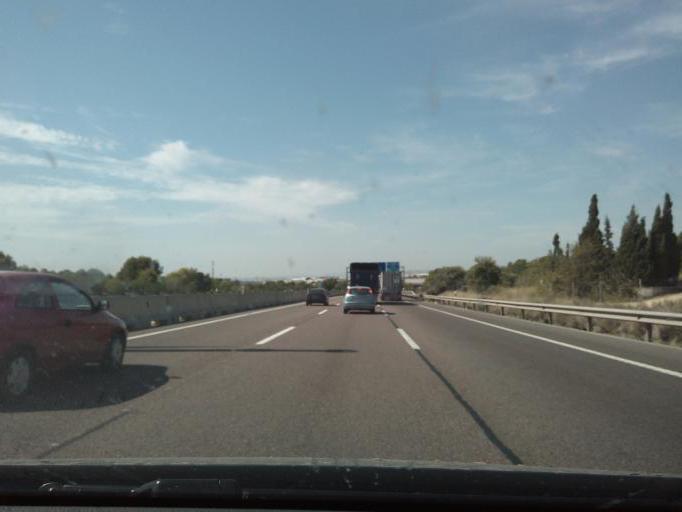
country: ES
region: Valencia
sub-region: Provincia de Valencia
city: Manises
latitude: 39.5311
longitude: -0.4626
